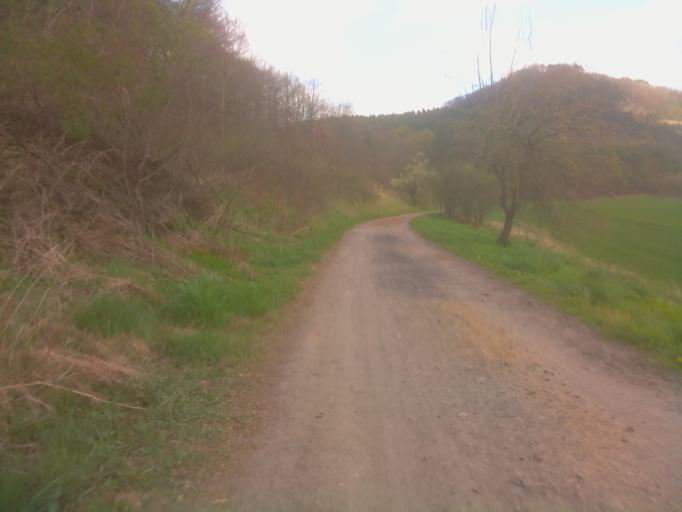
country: DE
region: Thuringia
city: Kahla
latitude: 50.8126
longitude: 11.5912
